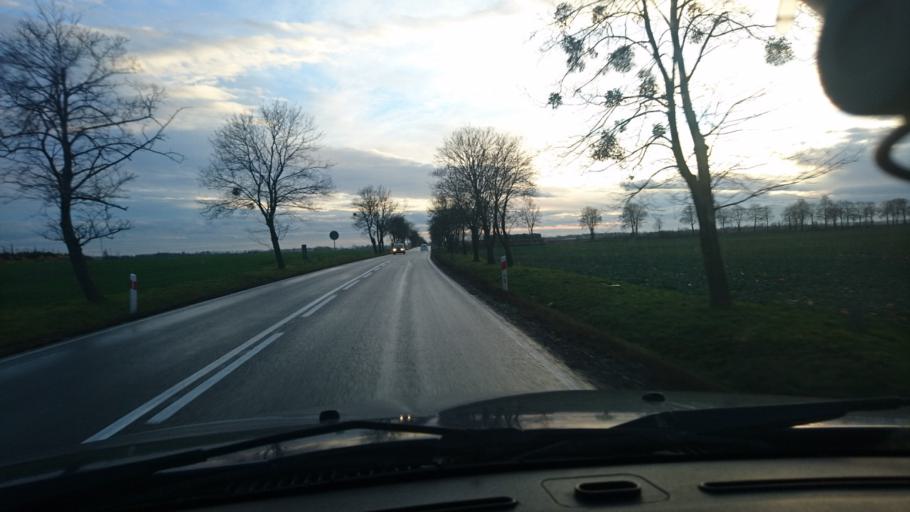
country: PL
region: Opole Voivodeship
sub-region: Powiat kluczborski
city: Byczyna
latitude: 51.0977
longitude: 18.2038
